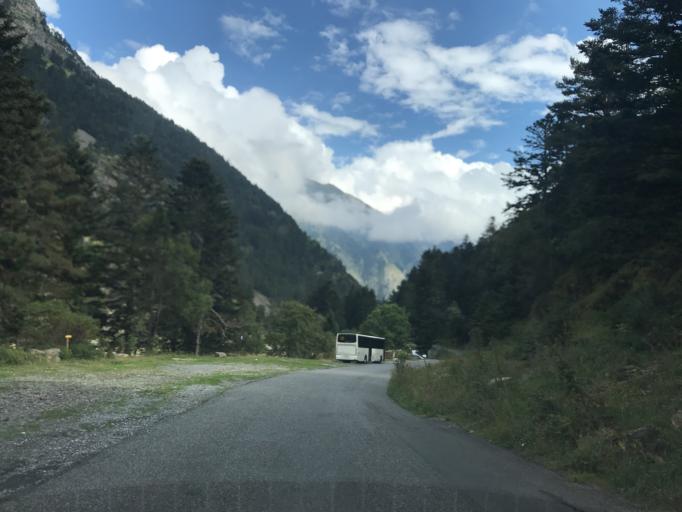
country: FR
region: Midi-Pyrenees
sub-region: Departement des Hautes-Pyrenees
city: Saint-Lary-Soulan
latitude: 42.8194
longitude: 0.1880
